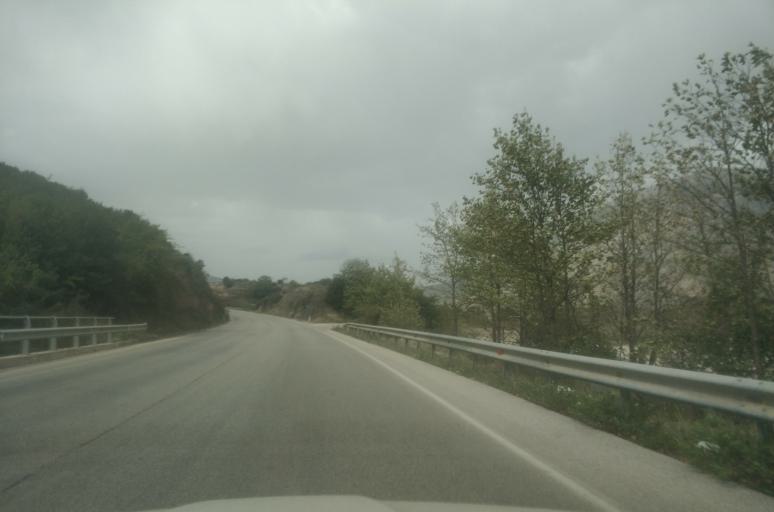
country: AL
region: Gjirokaster
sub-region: Rrethi i Tepelenes
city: Tepelene
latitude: 40.2646
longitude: 20.0513
